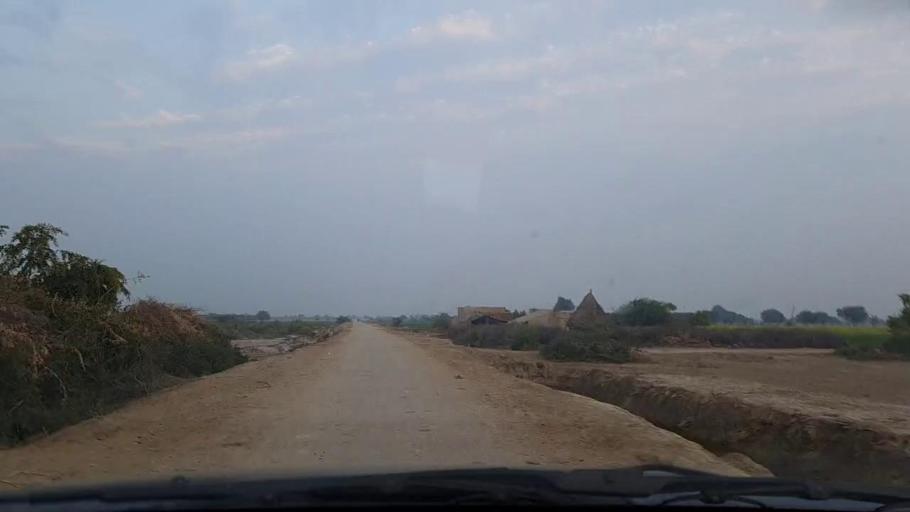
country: PK
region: Sindh
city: Pithoro
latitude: 25.6284
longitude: 69.4348
